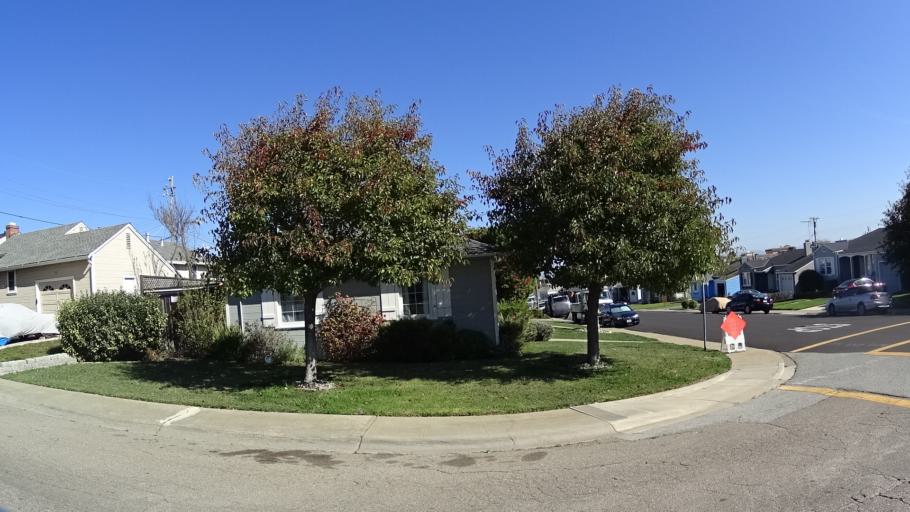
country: US
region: California
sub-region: San Mateo County
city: San Bruno
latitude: 37.6260
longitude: -122.4178
